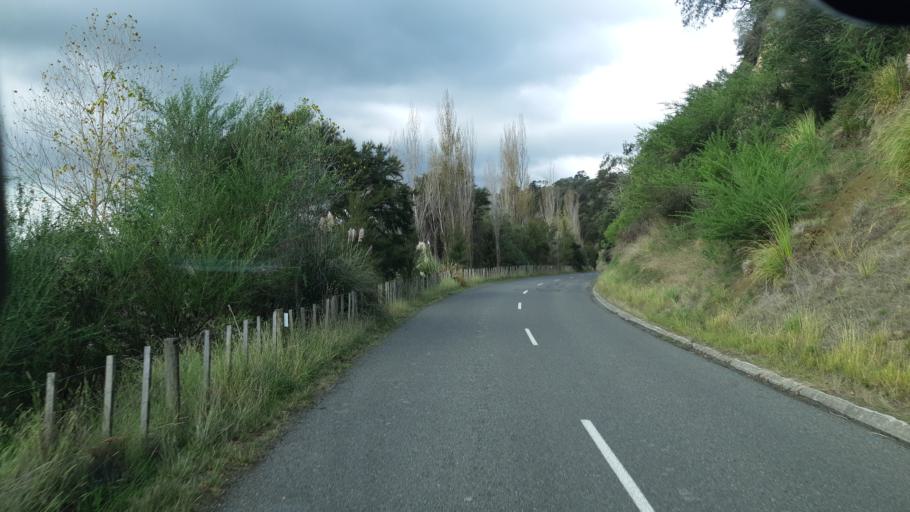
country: NZ
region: Manawatu-Wanganui
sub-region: Rangitikei District
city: Bulls
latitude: -40.0836
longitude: 175.4719
